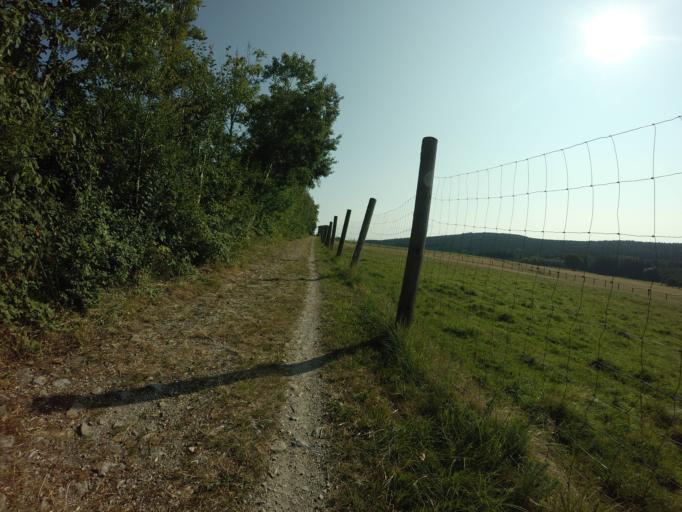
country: AT
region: Upper Austria
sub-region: Politischer Bezirk Urfahr-Umgebung
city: Bad Leonfelden
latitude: 48.5443
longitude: 14.3186
